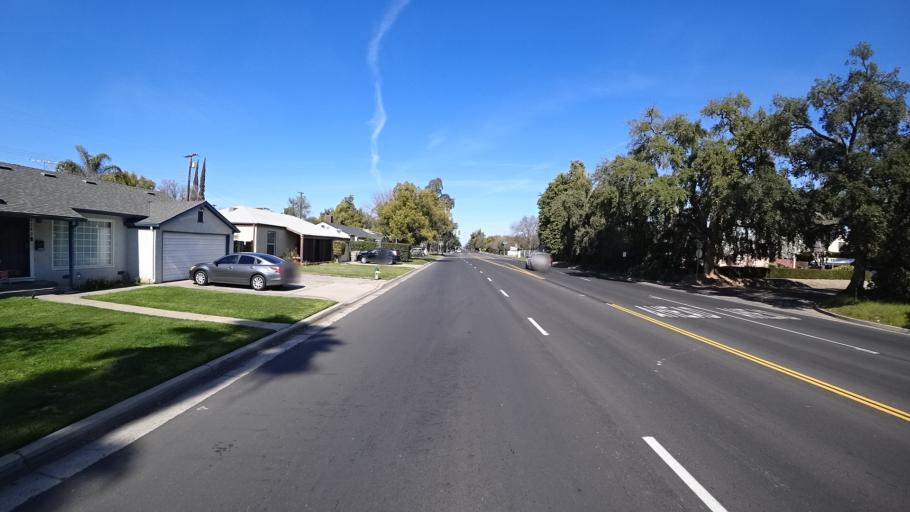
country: US
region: California
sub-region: Fresno County
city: Fresno
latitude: 36.7928
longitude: -119.8087
